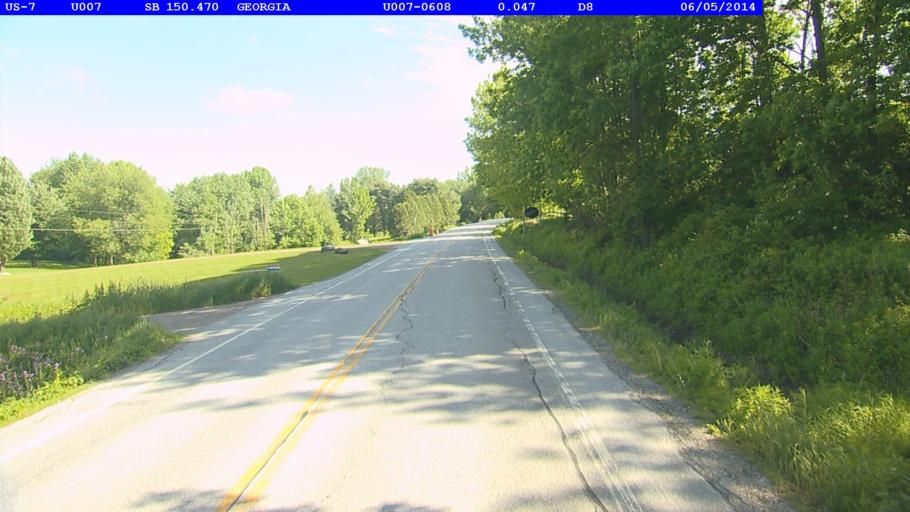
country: US
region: Vermont
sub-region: Chittenden County
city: Milton
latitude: 44.6798
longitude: -73.1112
